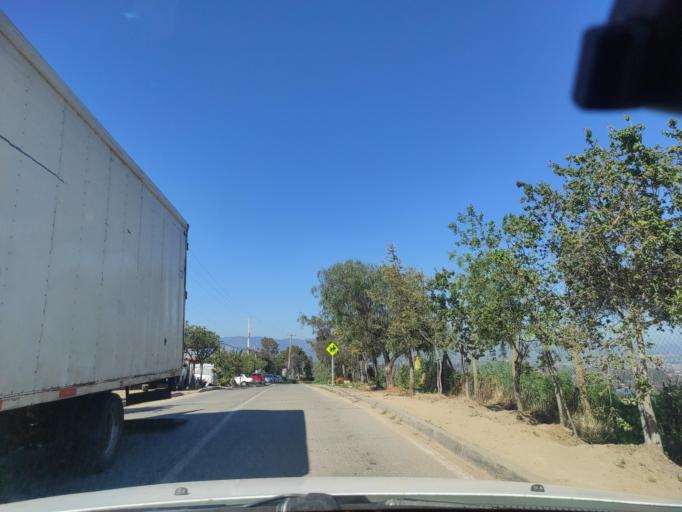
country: CL
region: Valparaiso
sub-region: Provincia de Marga Marga
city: Limache
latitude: -32.9892
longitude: -71.2252
